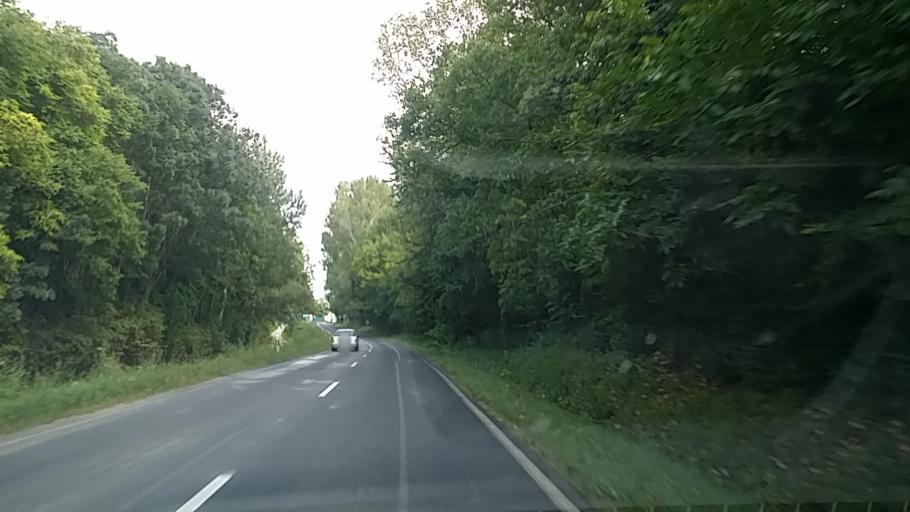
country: HU
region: Gyor-Moson-Sopron
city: Nagycenk
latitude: 47.6292
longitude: 16.7355
